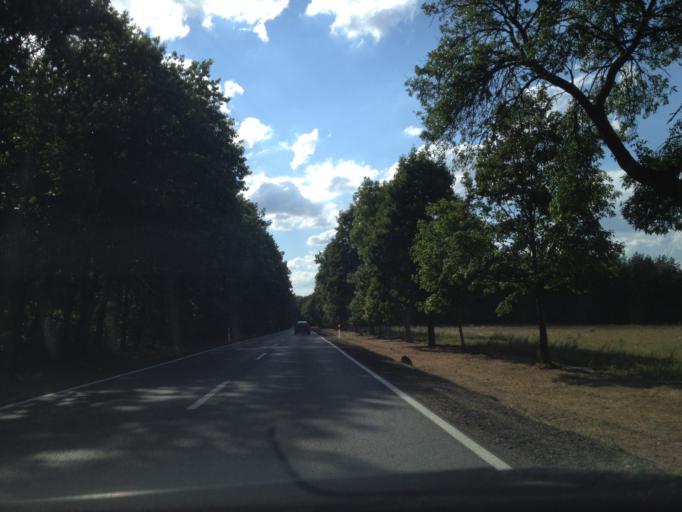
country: PL
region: Lubusz
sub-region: Powiat zarski
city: Sieniawa Zarska
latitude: 51.6304
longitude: 15.0457
